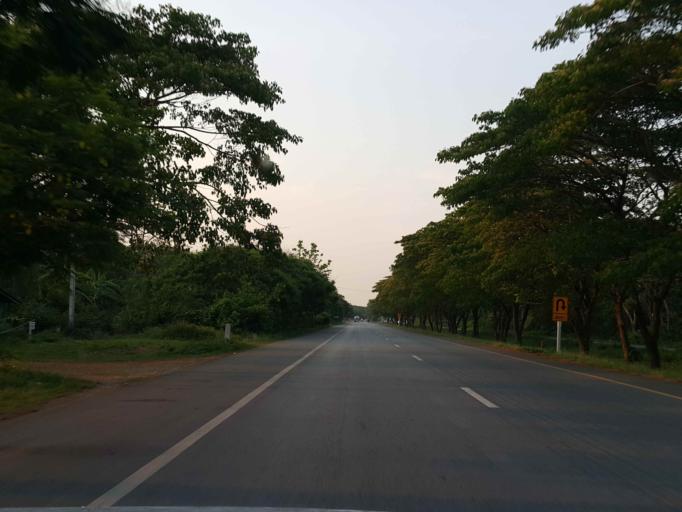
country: TH
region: Lampang
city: Sop Prap
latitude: 17.9064
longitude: 99.3414
